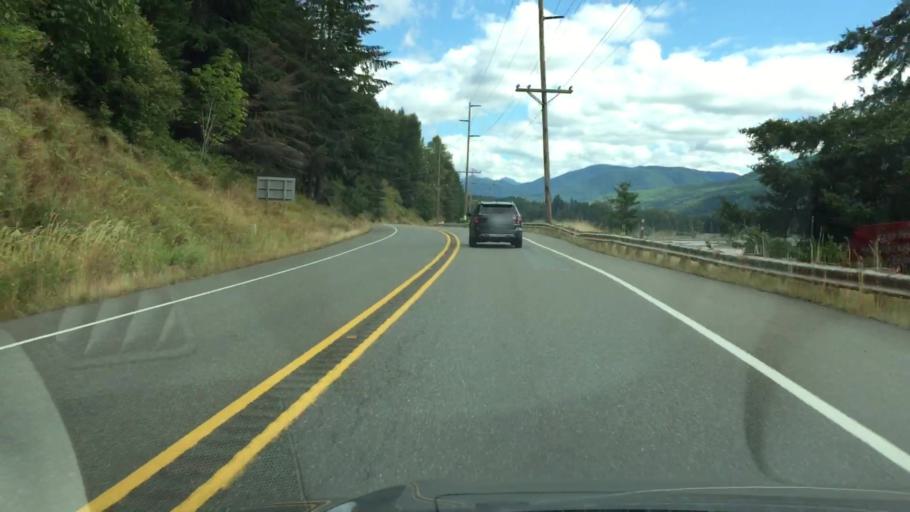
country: US
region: Washington
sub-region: Pierce County
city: Eatonville
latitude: 46.7713
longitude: -122.2122
